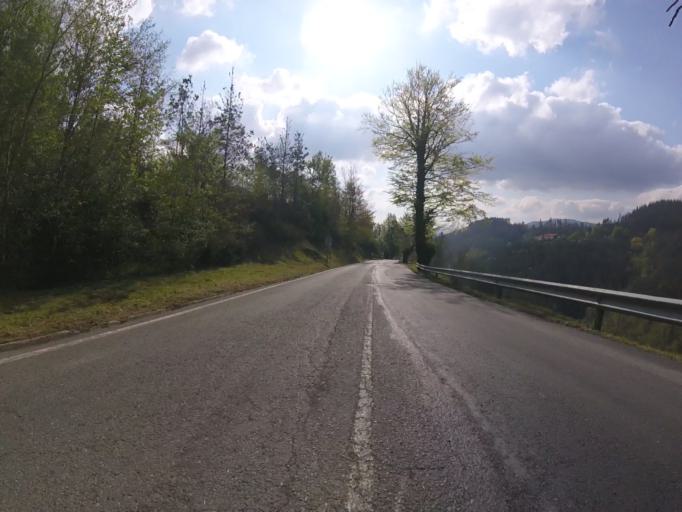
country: ES
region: Basque Country
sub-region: Provincia de Guipuzcoa
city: Azkoitia
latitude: 43.2018
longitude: -2.3541
